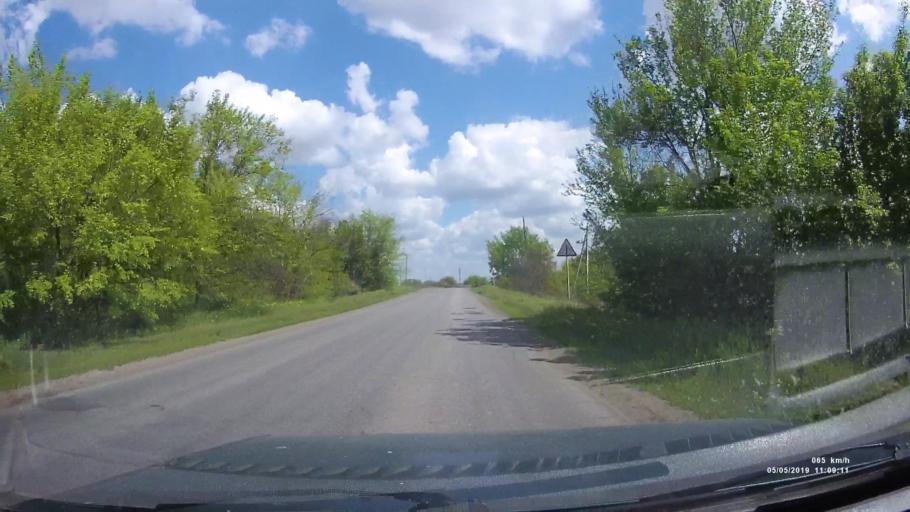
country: RU
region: Rostov
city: Ust'-Donetskiy
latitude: 47.7394
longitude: 40.9218
